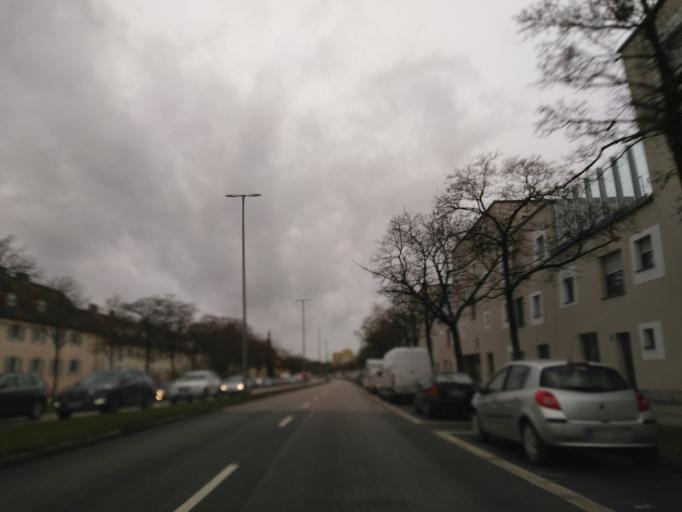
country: DE
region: Bavaria
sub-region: Upper Bavaria
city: Bogenhausen
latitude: 48.1192
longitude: 11.6292
